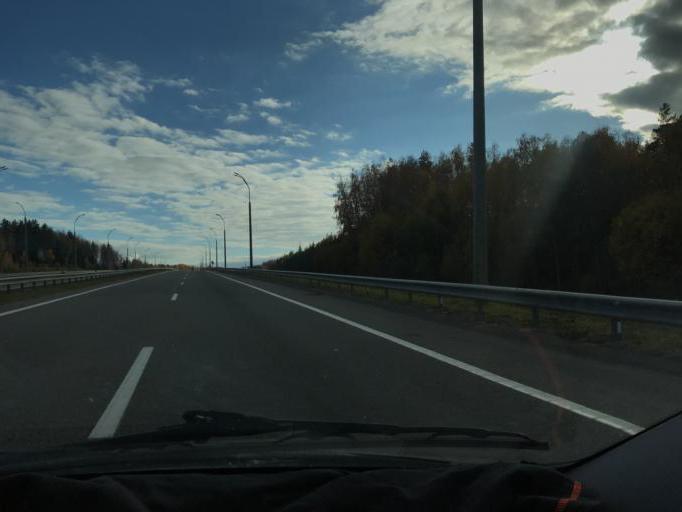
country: BY
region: Minsk
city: Lahoysk
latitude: 54.1811
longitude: 27.8178
